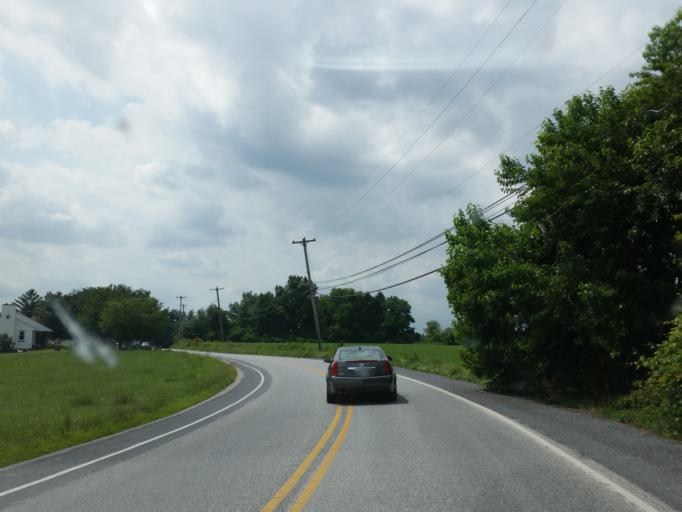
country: US
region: Delaware
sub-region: New Castle County
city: Newark
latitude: 39.7407
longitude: -75.8009
